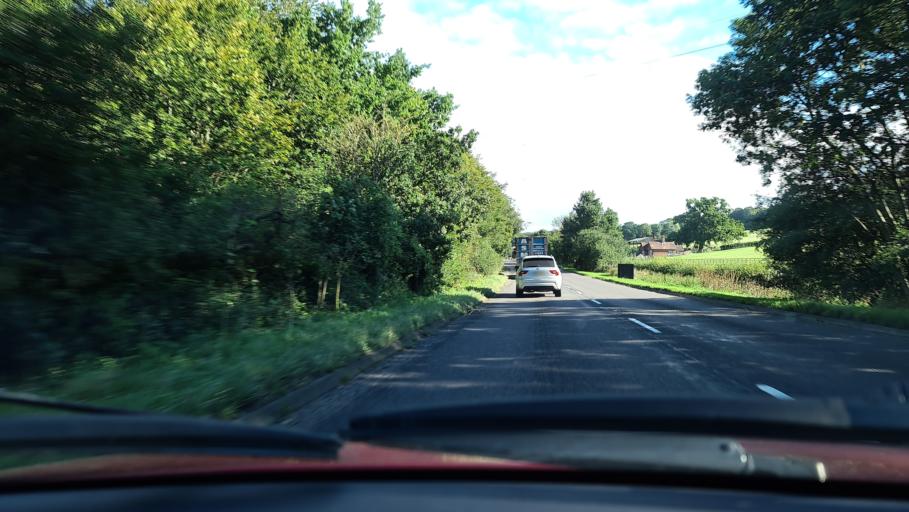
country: GB
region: England
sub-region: Buckinghamshire
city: Seer Green
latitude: 51.6290
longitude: -0.6216
